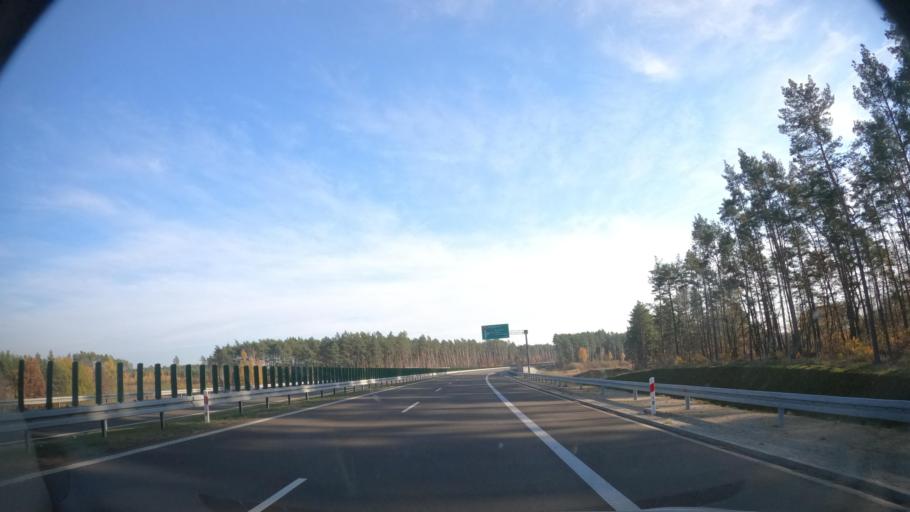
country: PL
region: West Pomeranian Voivodeship
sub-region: Powiat walecki
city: Walcz
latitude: 53.2928
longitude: 16.4980
